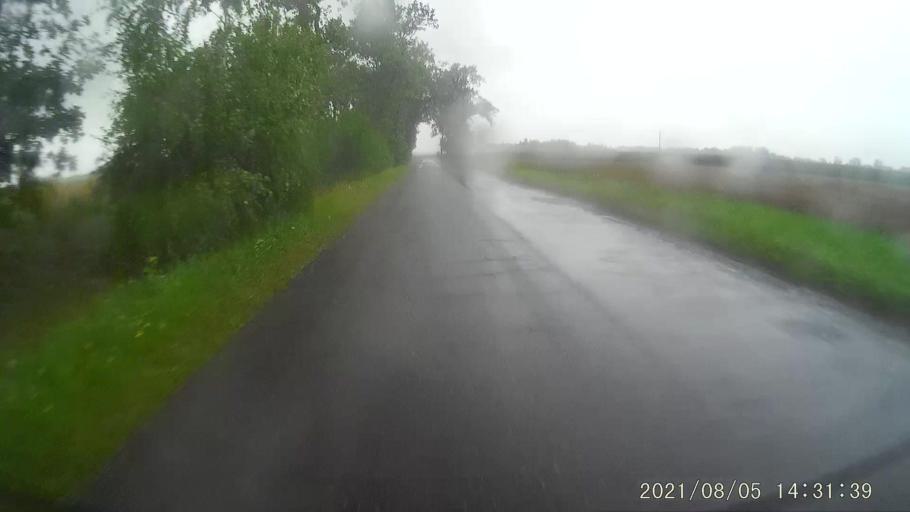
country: PL
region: Opole Voivodeship
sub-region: Powiat nyski
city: Korfantow
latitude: 50.4728
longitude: 17.5548
